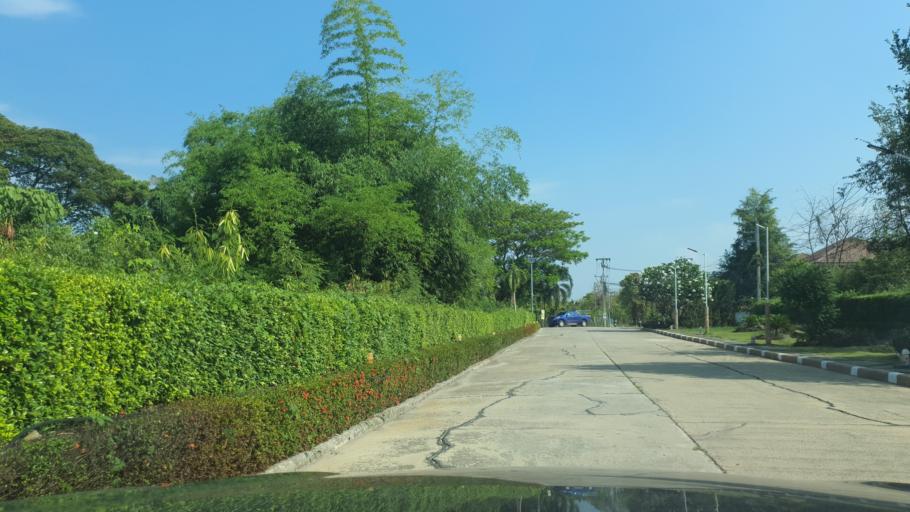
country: TH
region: Chiang Mai
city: Saraphi
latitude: 18.7426
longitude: 99.0626
